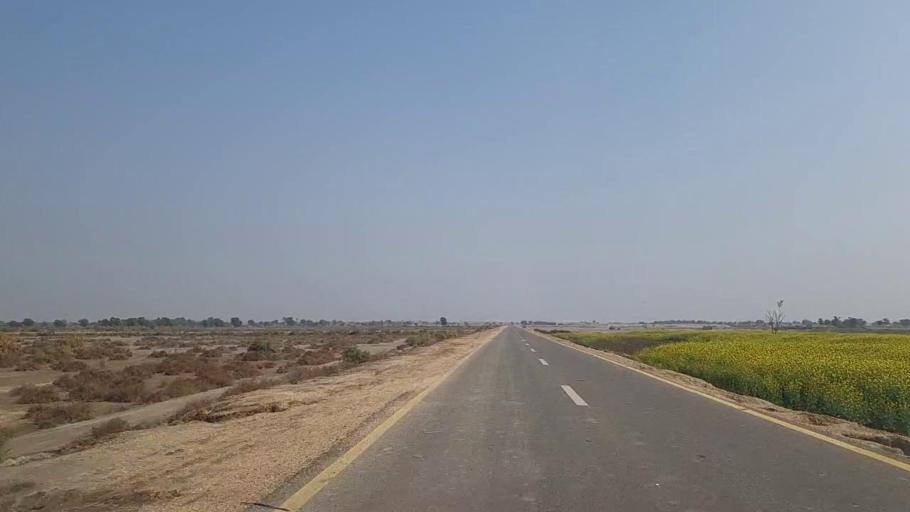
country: PK
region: Sindh
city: Jam Sahib
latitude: 26.3723
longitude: 68.5252
